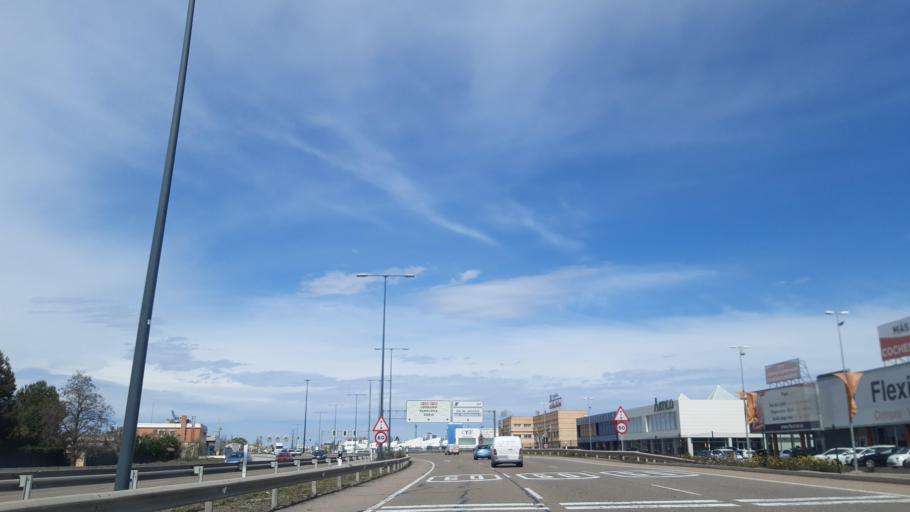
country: ES
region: Aragon
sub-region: Provincia de Zaragoza
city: Utebo
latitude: 41.6838
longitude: -0.9681
